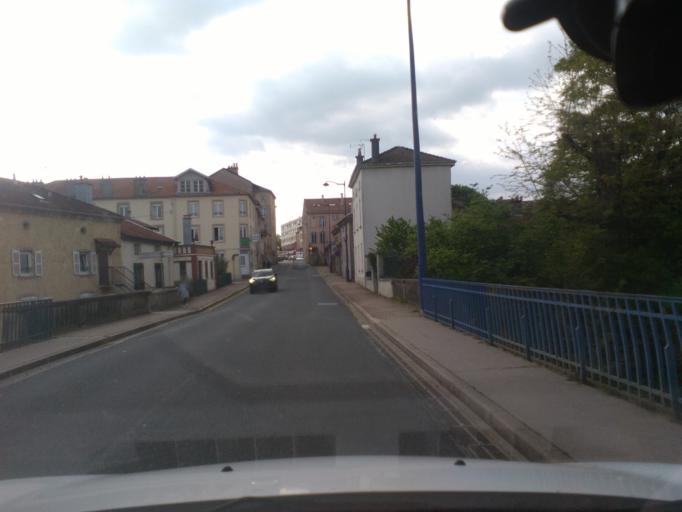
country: FR
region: Lorraine
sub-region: Departement des Vosges
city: Mirecourt
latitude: 48.3032
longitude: 6.1364
